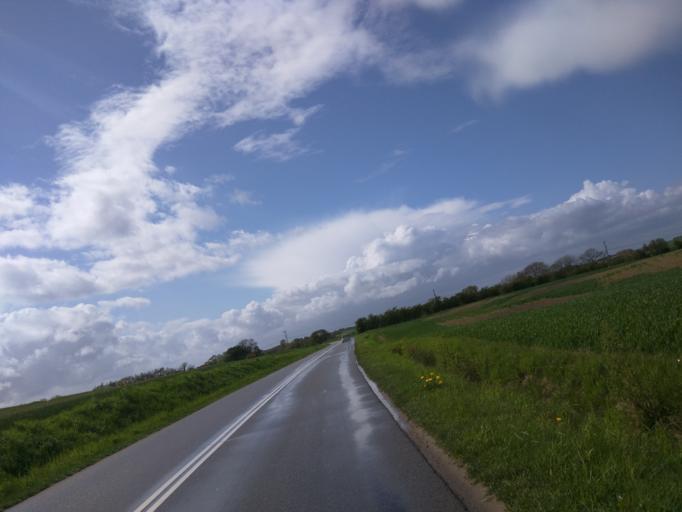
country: DK
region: Central Jutland
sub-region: Silkeborg Kommune
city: Kjellerup
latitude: 56.2758
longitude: 9.5102
